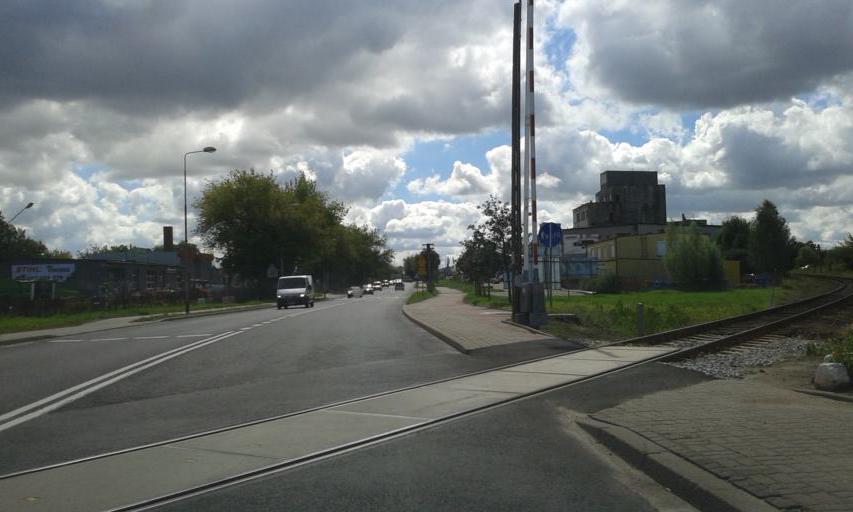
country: PL
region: West Pomeranian Voivodeship
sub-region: Powiat walecki
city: Walcz
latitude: 53.2676
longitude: 16.4862
